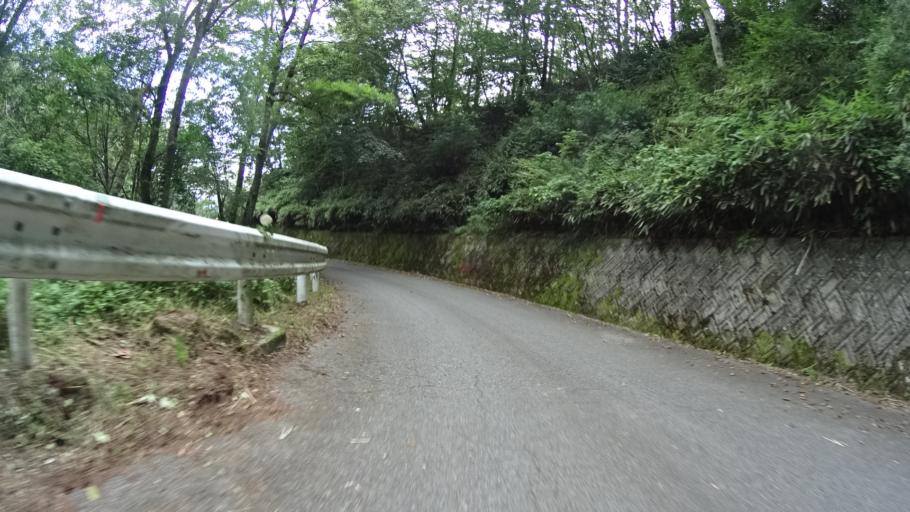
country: JP
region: Yamanashi
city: Nirasaki
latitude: 35.8065
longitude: 138.5273
